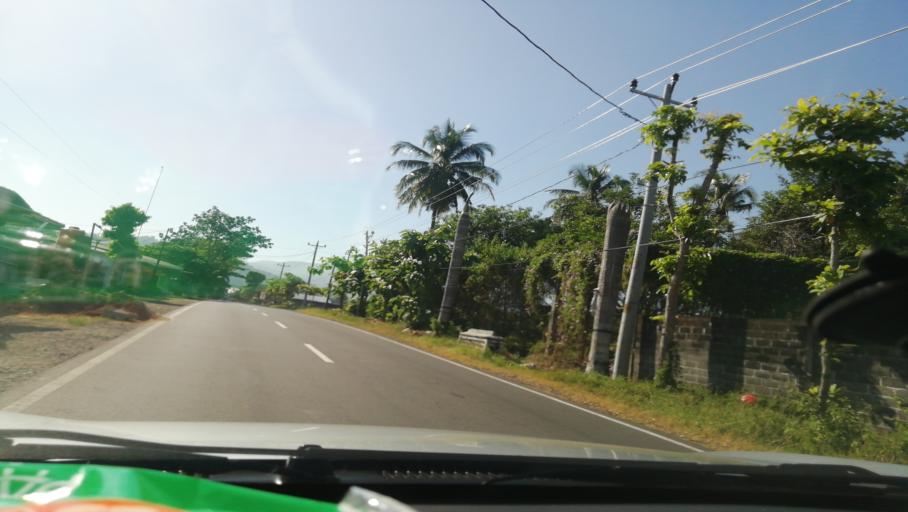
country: ID
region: Central Java
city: Kutoarjo
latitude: -7.7021
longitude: 110.0157
